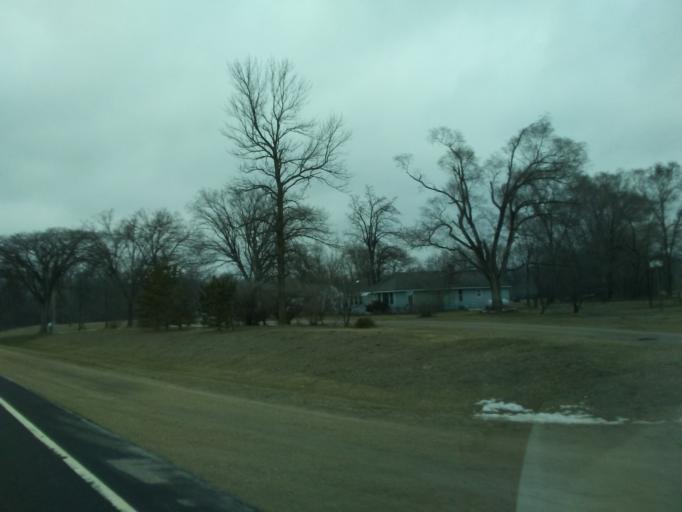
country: US
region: Wisconsin
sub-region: Sauk County
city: Spring Green
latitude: 43.1998
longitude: -90.2418
